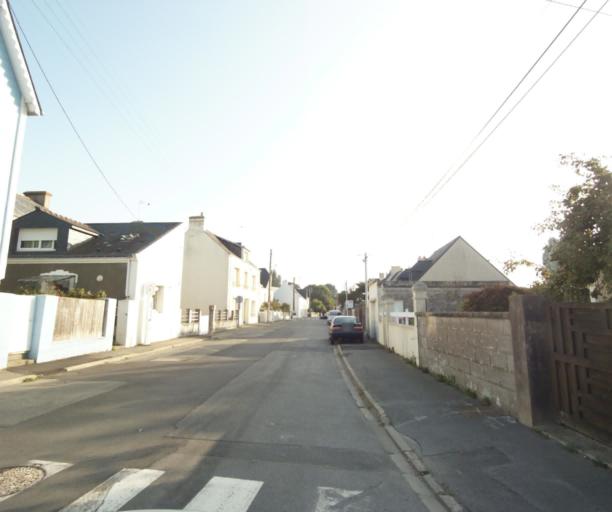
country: FR
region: Brittany
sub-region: Departement du Morbihan
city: Riantec
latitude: 47.7119
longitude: -3.3096
